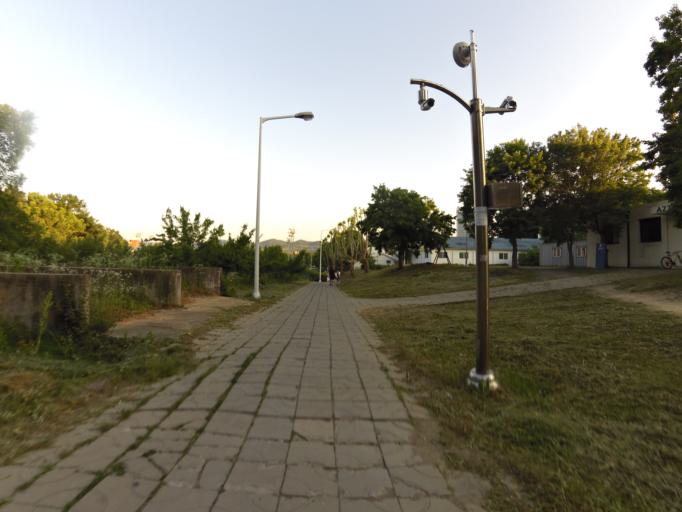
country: KR
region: Gyeongsangbuk-do
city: Gyeongsan-si
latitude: 35.8366
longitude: 128.7597
